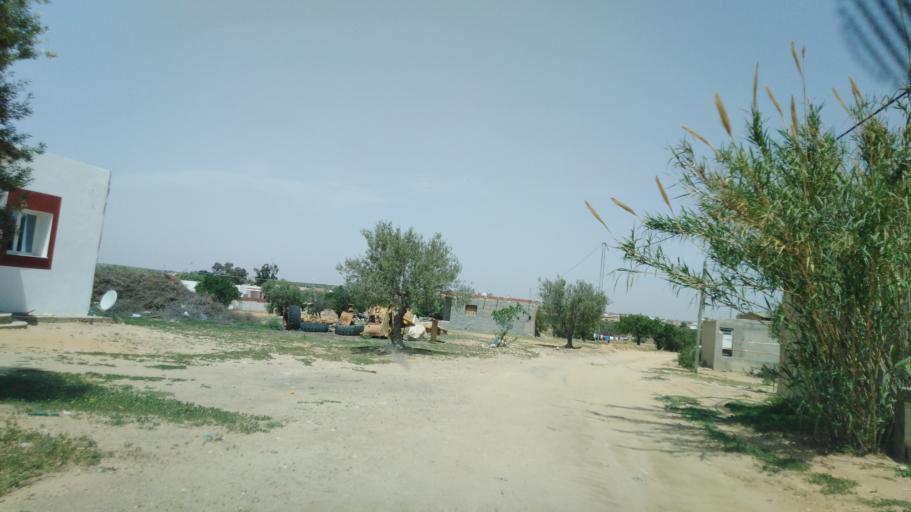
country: TN
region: Safaqis
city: Sfax
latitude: 34.7306
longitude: 10.5543
